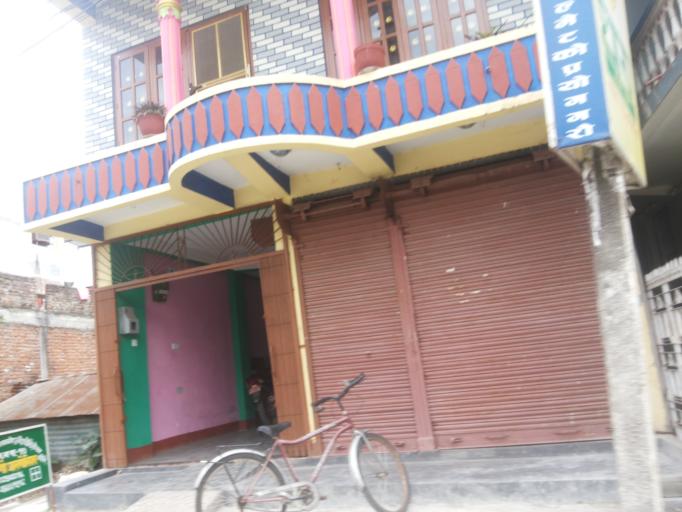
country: NP
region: Central Region
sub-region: Narayani Zone
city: Bharatpur
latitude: 27.6909
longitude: 84.4368
